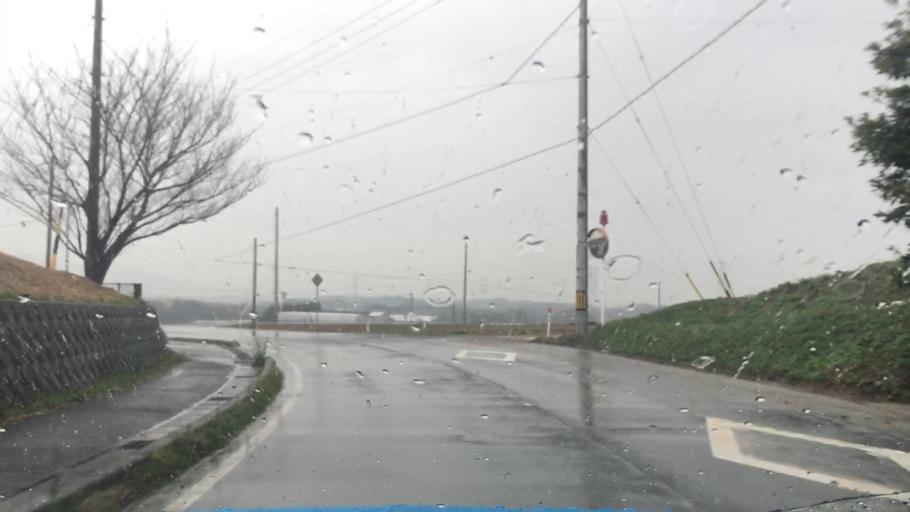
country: JP
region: Aichi
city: Tahara
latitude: 34.6479
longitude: 137.3059
